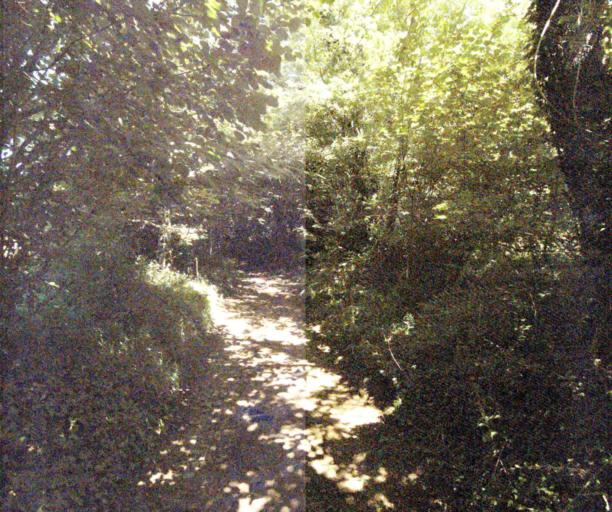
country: FR
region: Midi-Pyrenees
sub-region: Departement du Tarn
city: Dourgne
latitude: 43.4226
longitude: 2.1638
